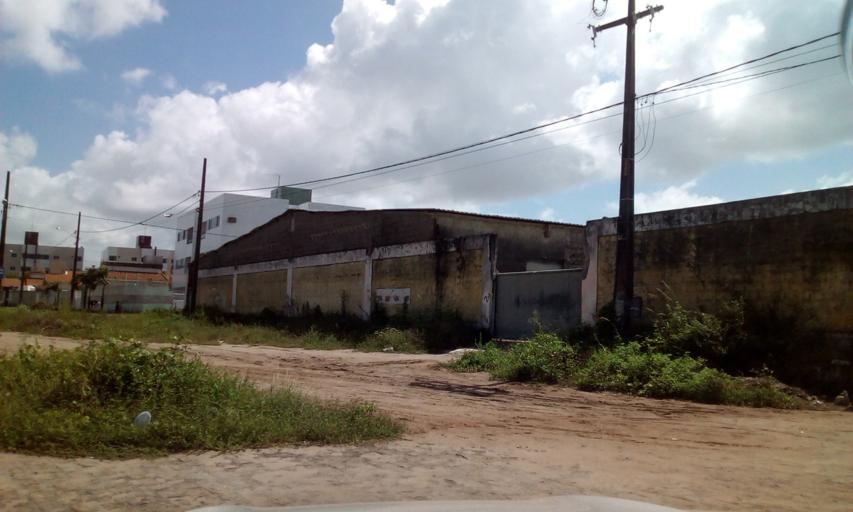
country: BR
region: Paraiba
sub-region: Conde
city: Conde
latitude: -7.2206
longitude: -34.8323
